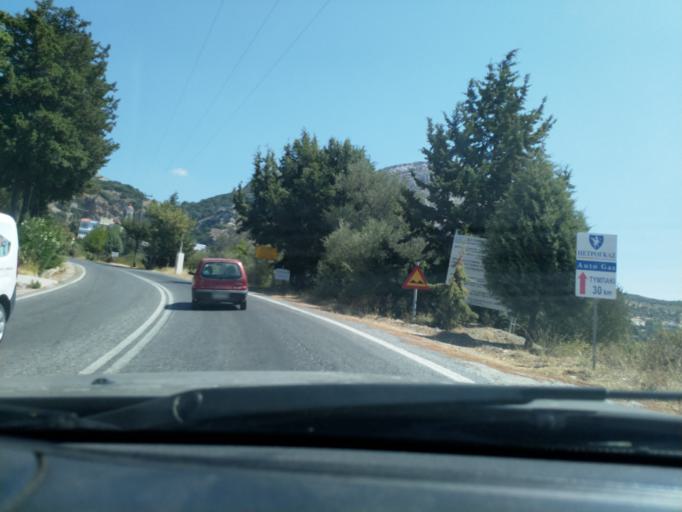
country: GR
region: Crete
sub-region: Nomos Rethymnis
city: Agia Foteini
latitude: 35.2194
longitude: 24.5281
